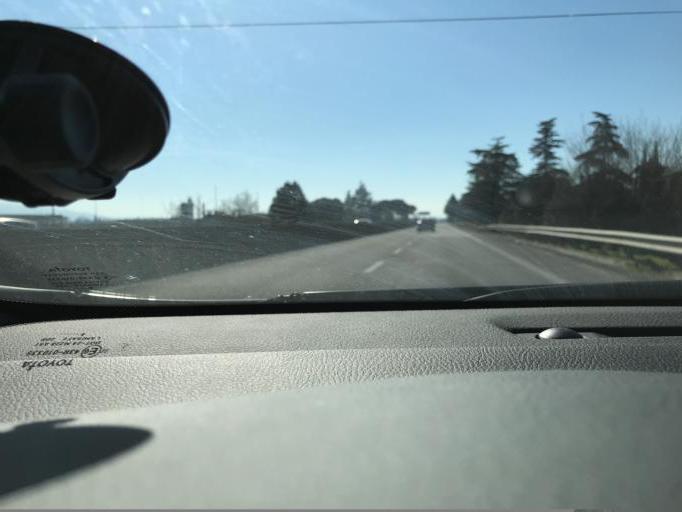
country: IT
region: Umbria
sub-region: Provincia di Perugia
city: San Martino in Campo
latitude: 43.0722
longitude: 12.4185
